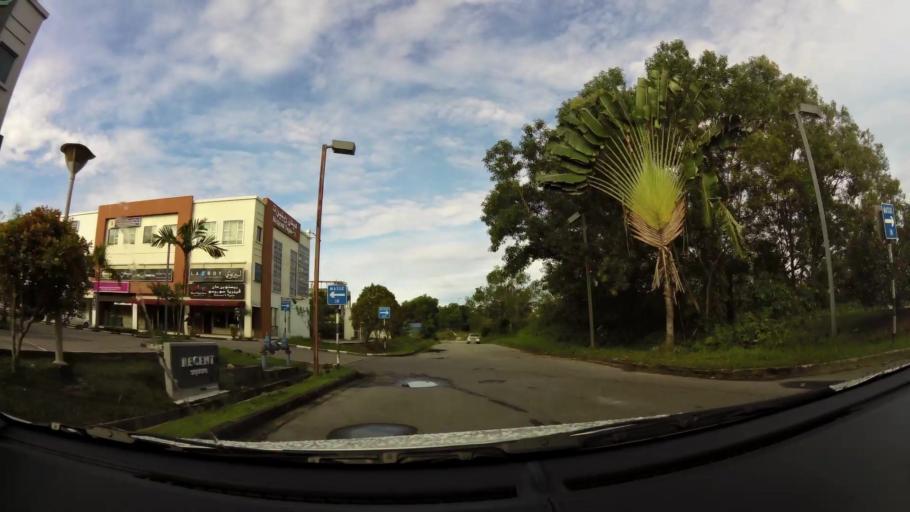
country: BN
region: Brunei and Muara
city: Bandar Seri Begawan
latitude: 4.9043
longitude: 114.9211
